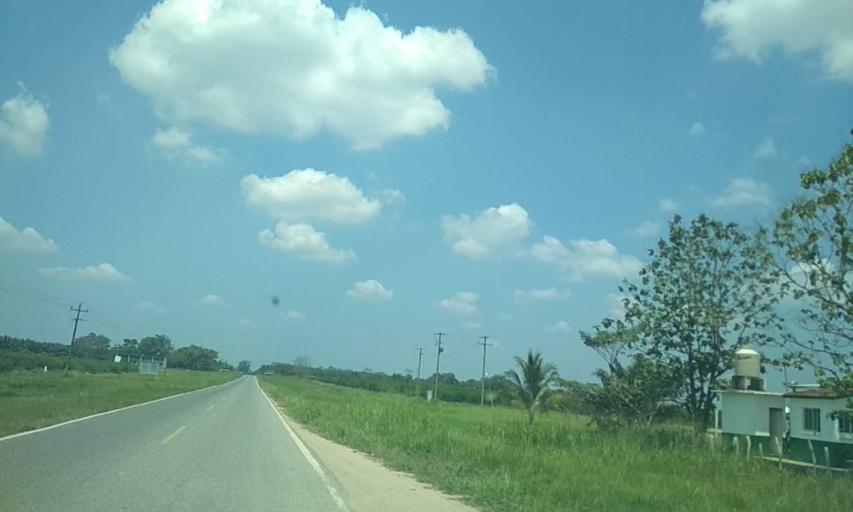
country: MX
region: Tabasco
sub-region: Huimanguillo
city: Huapacal 1ra. Seccion
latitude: 17.7512
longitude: -93.6660
